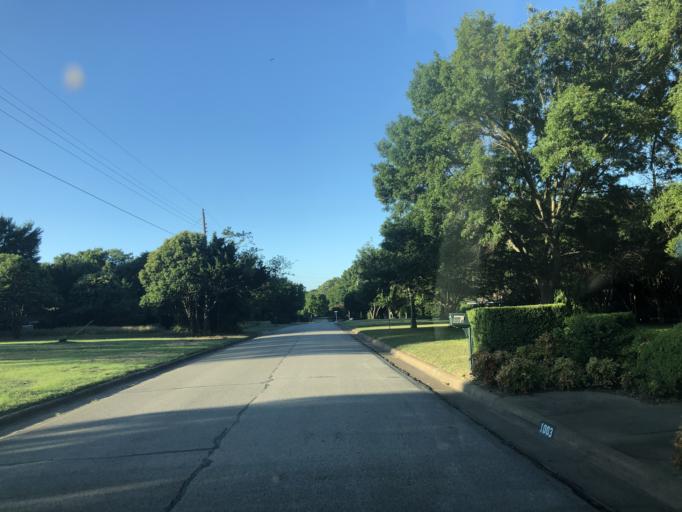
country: US
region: Texas
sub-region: Dallas County
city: Duncanville
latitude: 32.6419
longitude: -96.9382
